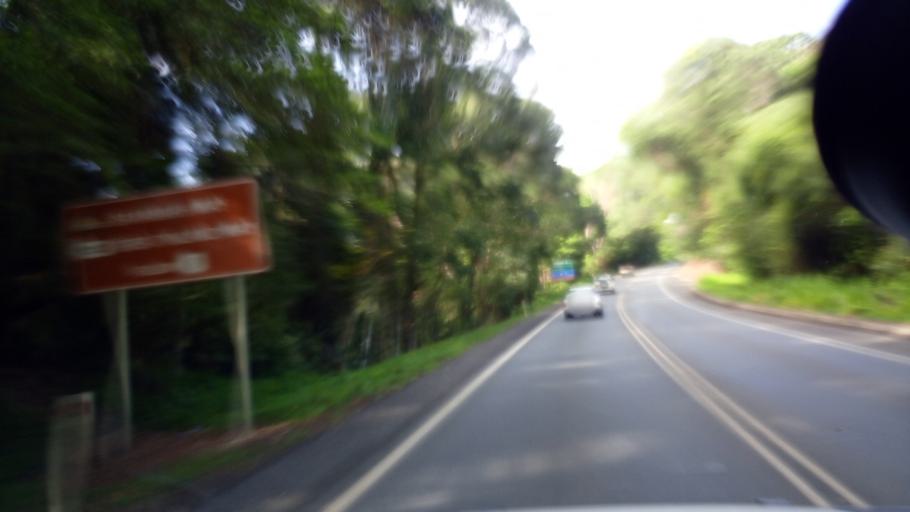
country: AU
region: Queensland
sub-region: Tablelands
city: Kuranda
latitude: -16.8192
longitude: 145.6314
